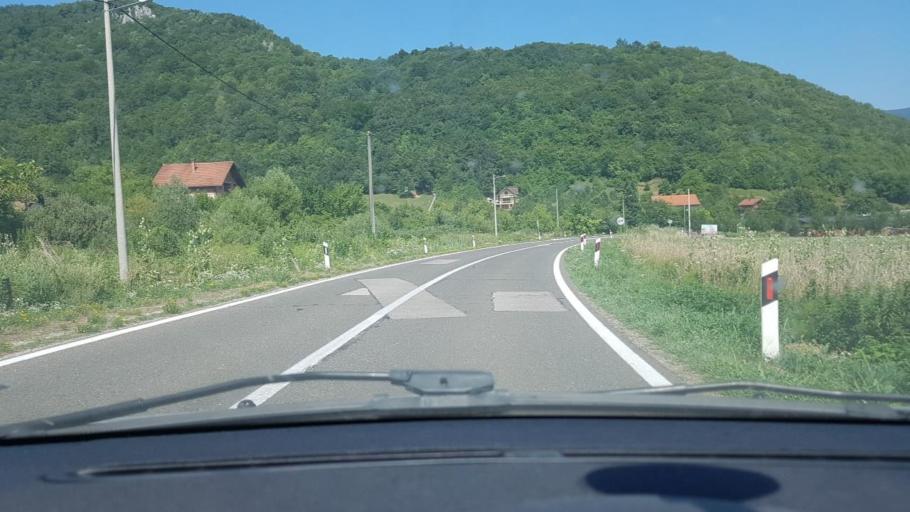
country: BA
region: Federation of Bosnia and Herzegovina
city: Bihac
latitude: 44.7518
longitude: 15.9295
